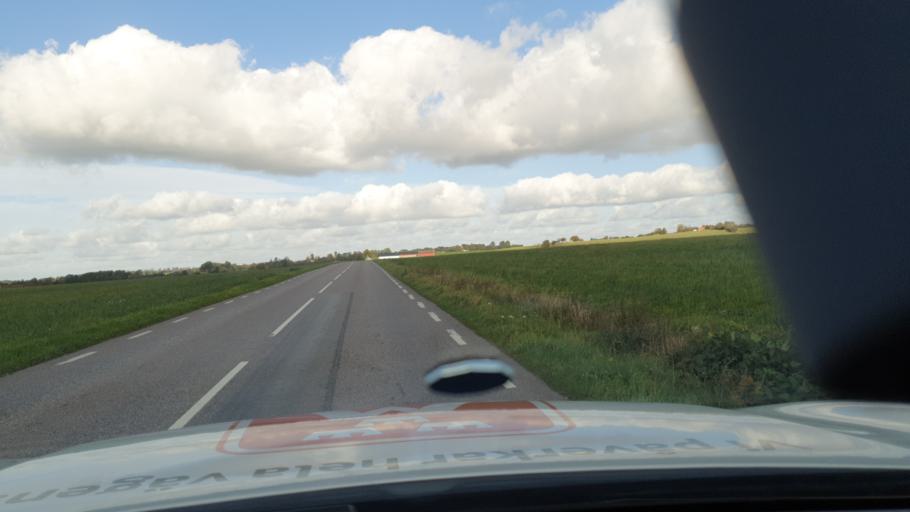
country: SE
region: Skane
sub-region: Ystads Kommun
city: Kopingebro
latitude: 55.4853
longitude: 13.9501
